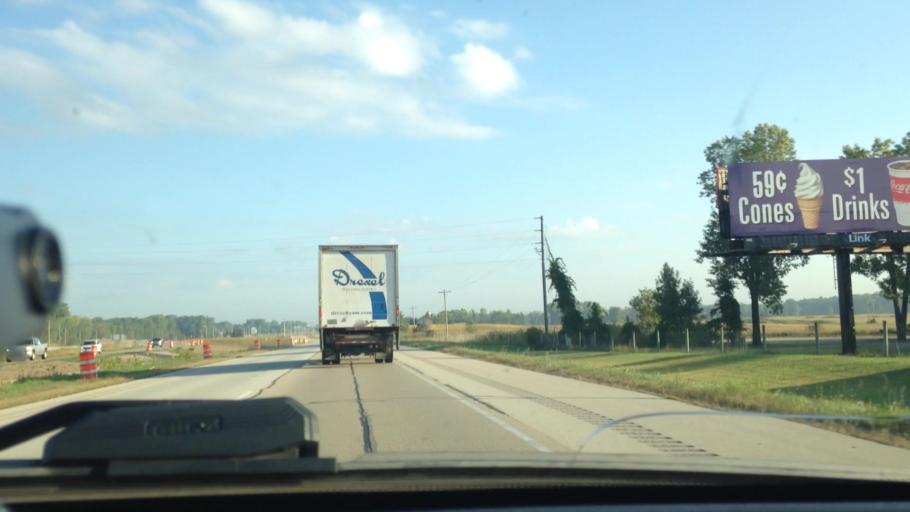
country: US
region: Wisconsin
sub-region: Brown County
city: Suamico
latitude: 44.7347
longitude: -88.0506
